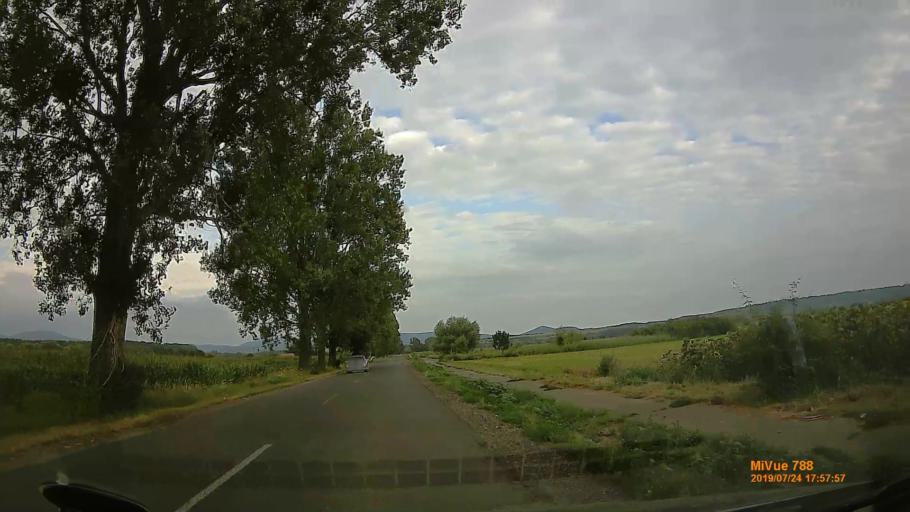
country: HU
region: Borsod-Abauj-Zemplen
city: Encs
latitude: 48.3288
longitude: 21.1411
